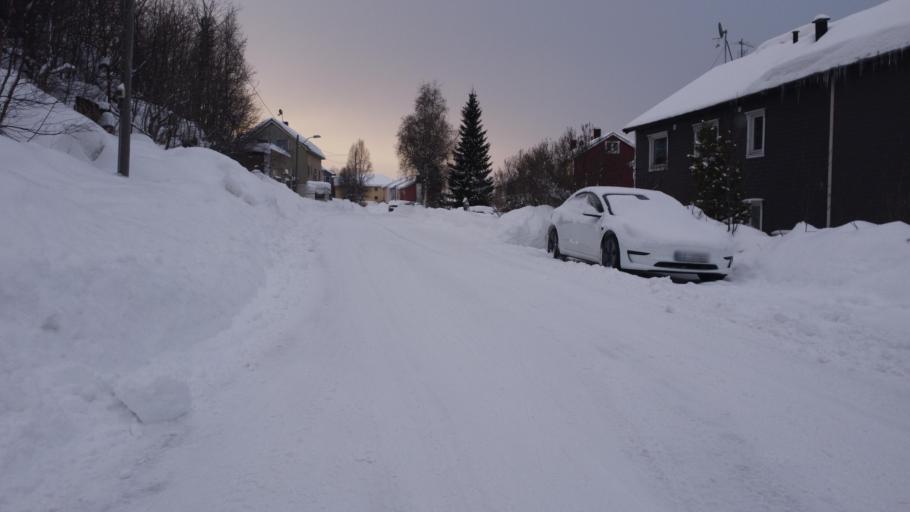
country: NO
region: Nordland
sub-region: Rana
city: Mo i Rana
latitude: 66.3157
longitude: 14.1419
